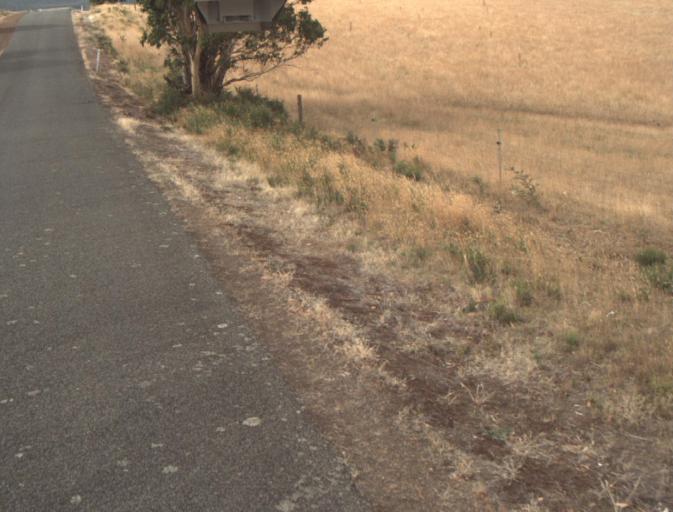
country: AU
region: Tasmania
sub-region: Northern Midlands
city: Evandale
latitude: -41.4709
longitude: 147.4964
